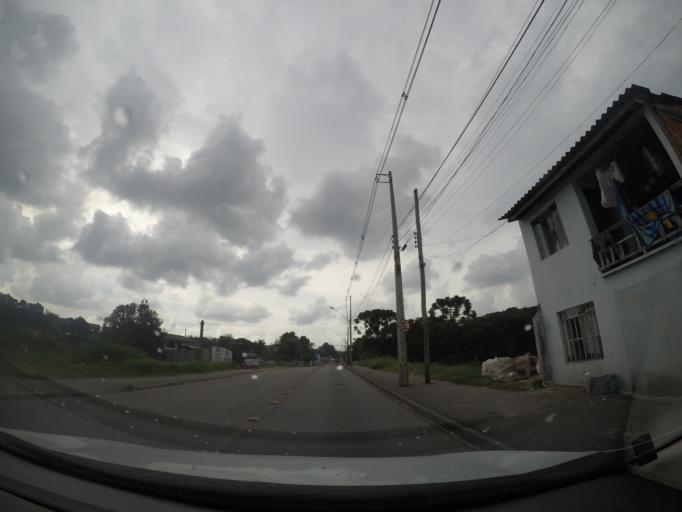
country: BR
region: Parana
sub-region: Sao Jose Dos Pinhais
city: Sao Jose dos Pinhais
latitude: -25.5485
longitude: -49.2460
